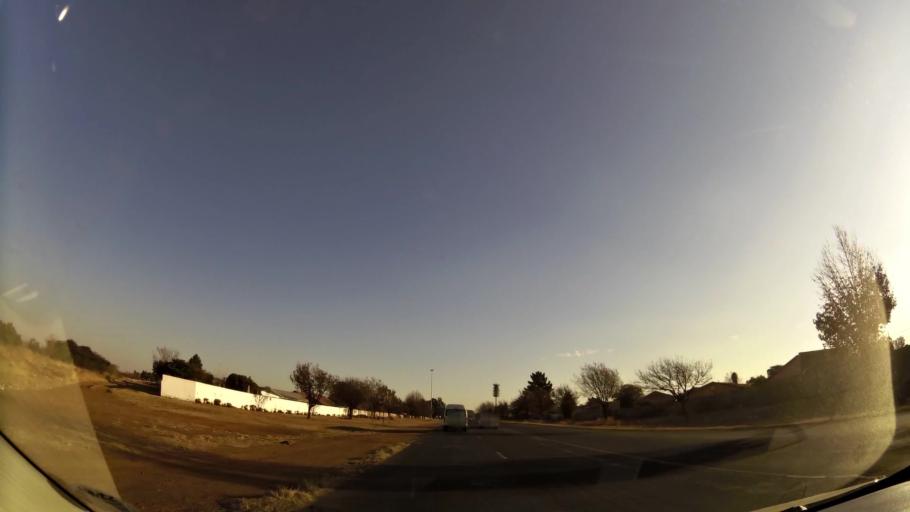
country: ZA
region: Gauteng
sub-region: West Rand District Municipality
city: Randfontein
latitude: -26.2080
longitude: 27.6587
